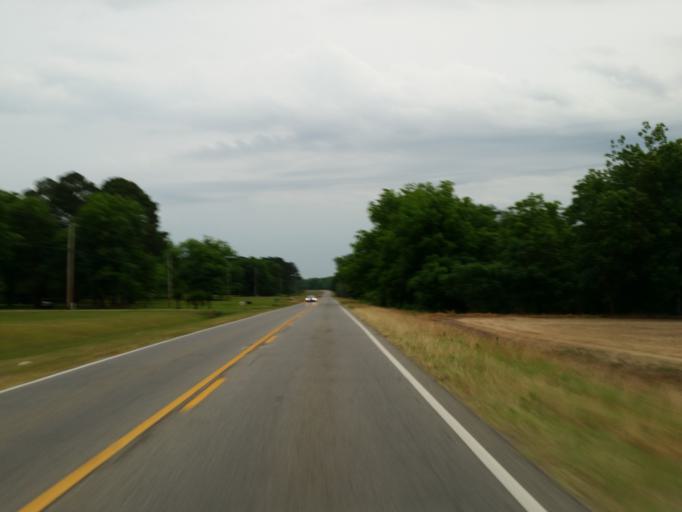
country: US
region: Georgia
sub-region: Crisp County
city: Cordele
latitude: 32.0107
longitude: -83.7928
